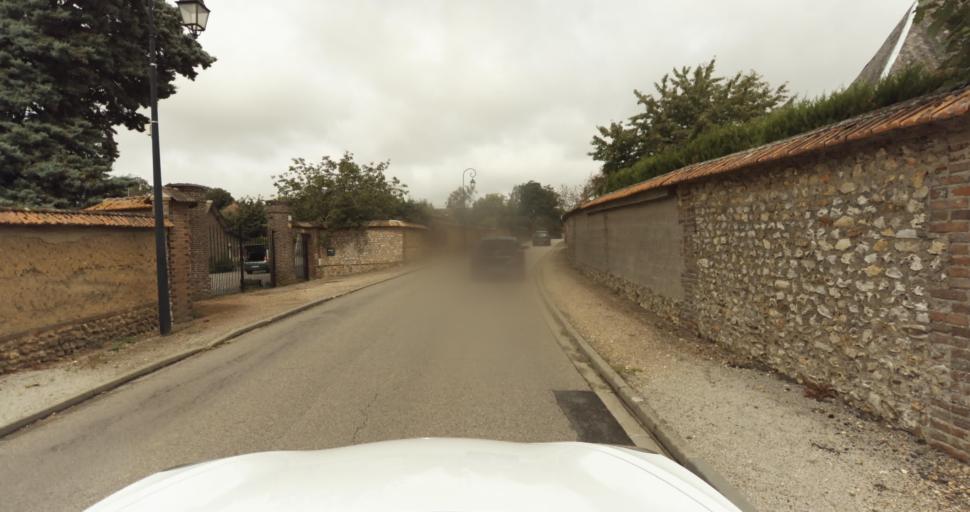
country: FR
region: Haute-Normandie
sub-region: Departement de l'Eure
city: Aviron
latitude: 49.0464
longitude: 1.0870
